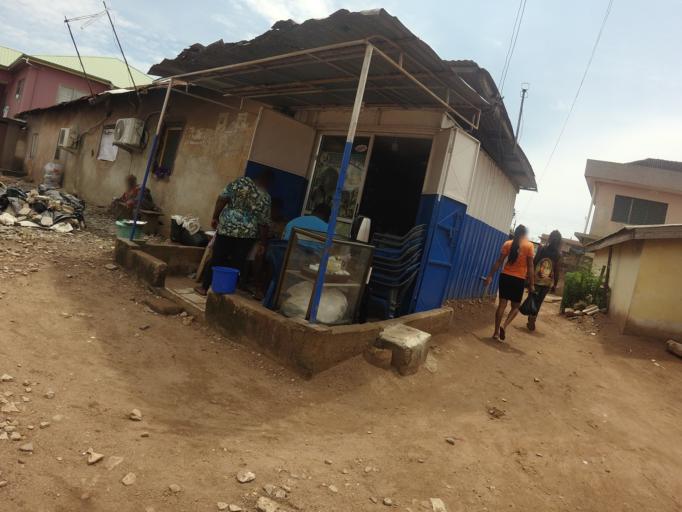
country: GH
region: Greater Accra
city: Accra
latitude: 5.5865
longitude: -0.2046
